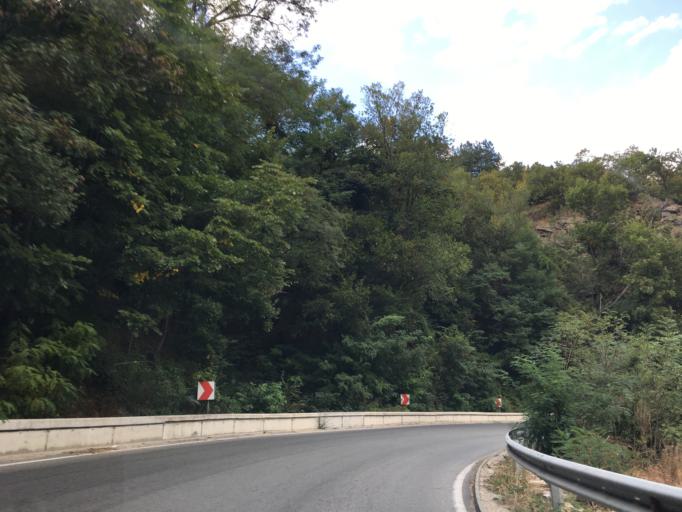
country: BG
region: Pazardzhik
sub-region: Obshtina Septemvri
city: Septemvri
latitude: 42.1313
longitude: 24.1233
